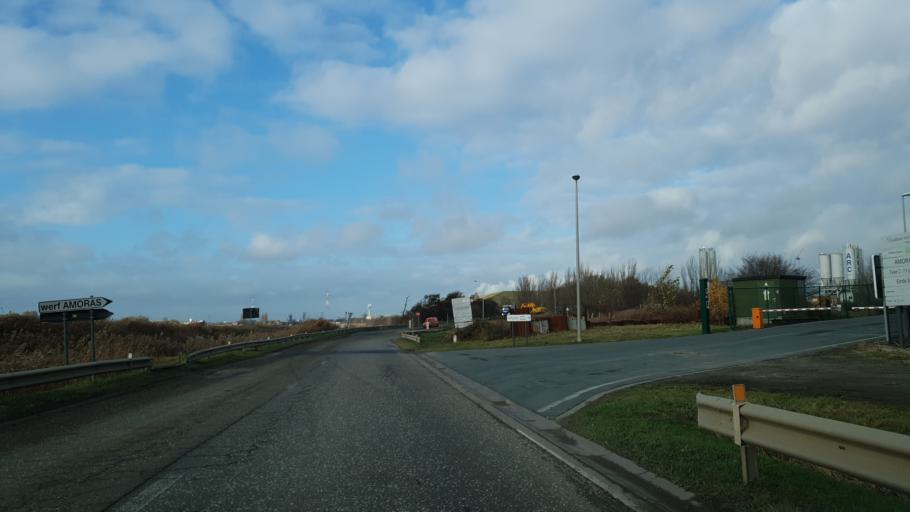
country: BE
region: Flanders
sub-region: Provincie Antwerpen
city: Stabroek
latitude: 51.3036
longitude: 4.3636
